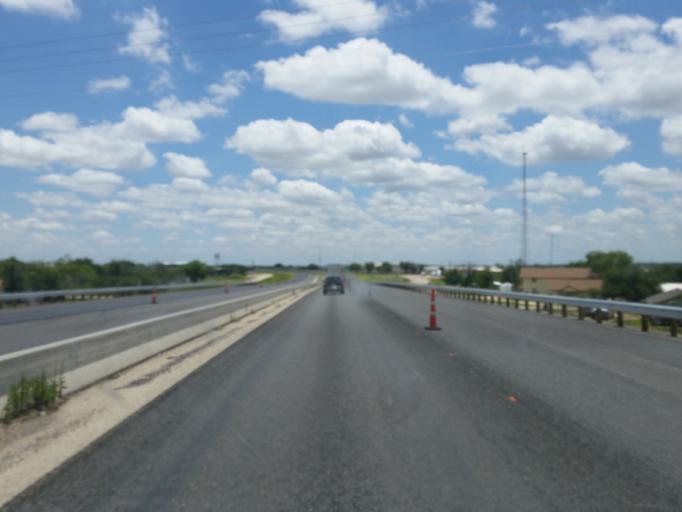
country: US
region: Texas
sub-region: Scurry County
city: Snyder
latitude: 32.7469
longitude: -100.9242
